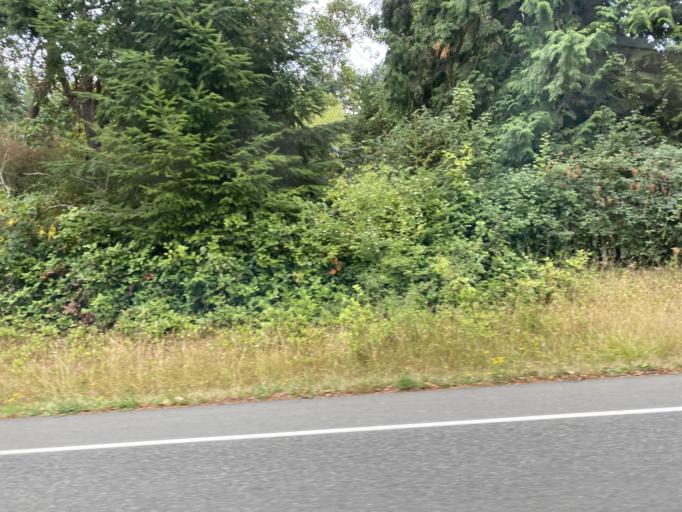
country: US
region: Washington
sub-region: Island County
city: Coupeville
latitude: 48.2139
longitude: -122.7103
